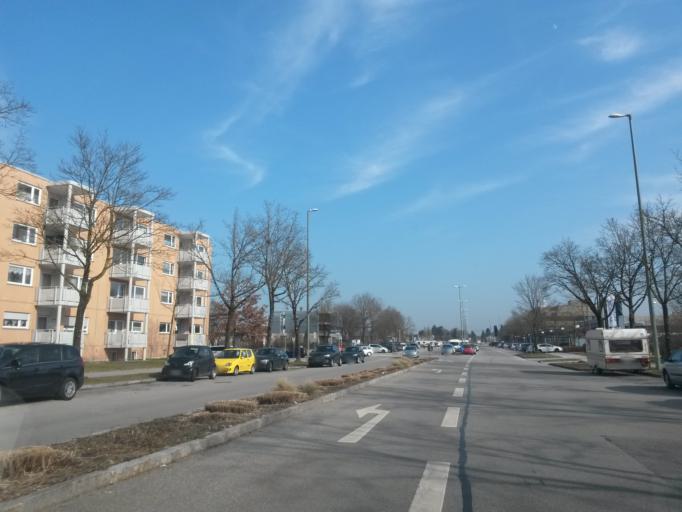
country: DE
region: Bavaria
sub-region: Upper Bavaria
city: Neubiberg
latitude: 48.0917
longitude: 11.6533
